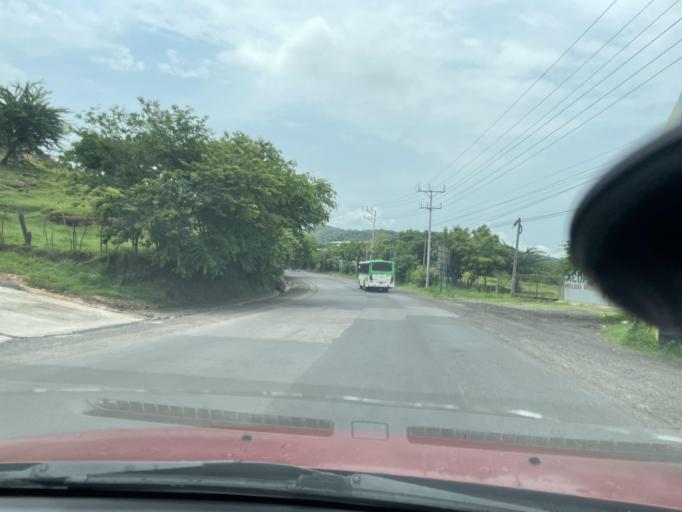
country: SV
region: La Union
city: Santa Rosa de Lima
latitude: 13.6191
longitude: -87.8616
